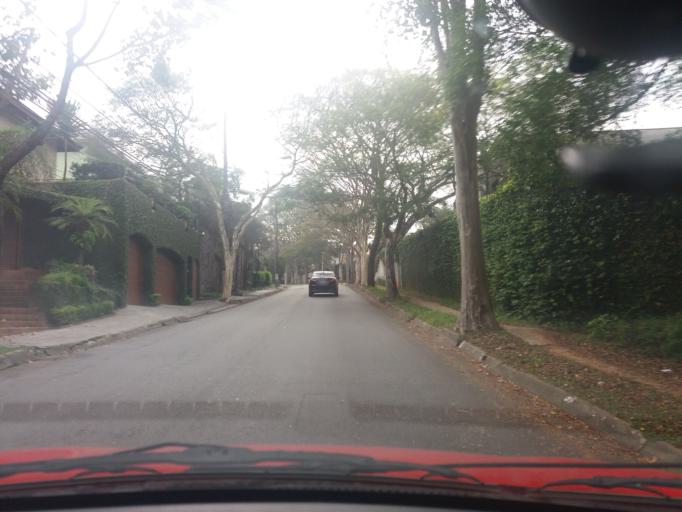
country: BR
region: Sao Paulo
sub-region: Taboao Da Serra
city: Taboao da Serra
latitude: -23.5931
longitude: -46.7137
